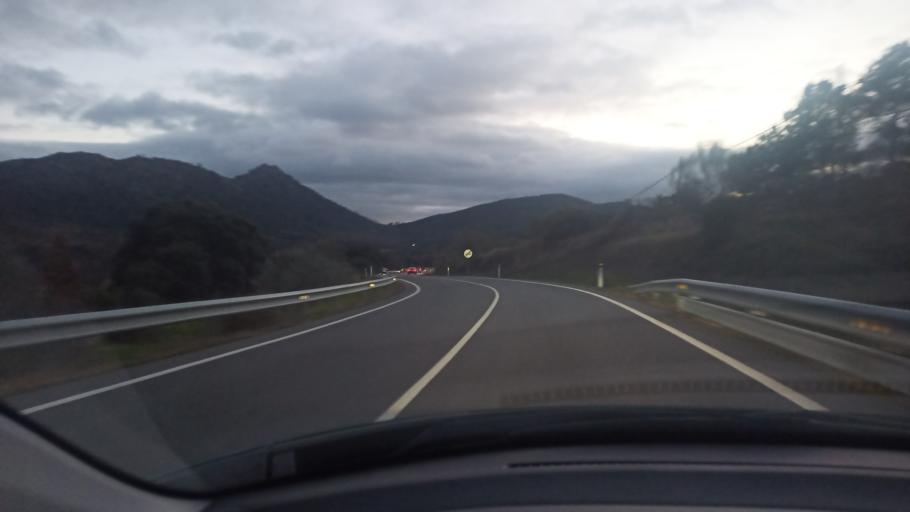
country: ES
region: Madrid
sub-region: Provincia de Madrid
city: Robledo de Chavela
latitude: 40.4809
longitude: -4.2545
